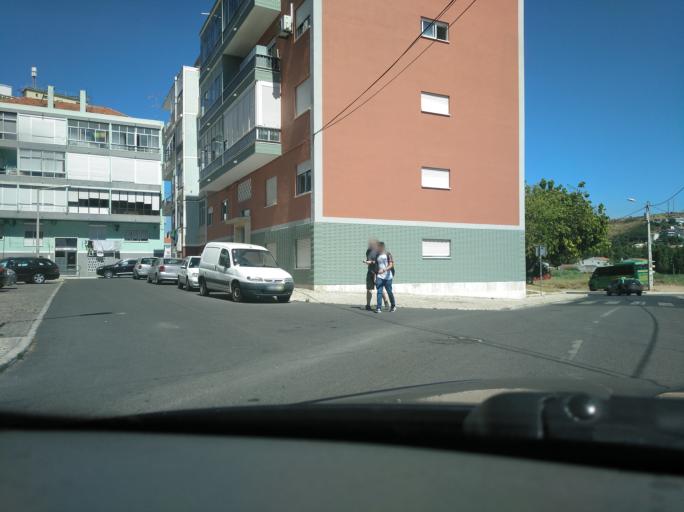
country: PT
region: Lisbon
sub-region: Odivelas
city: Odivelas
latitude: 38.7855
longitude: -9.1830
